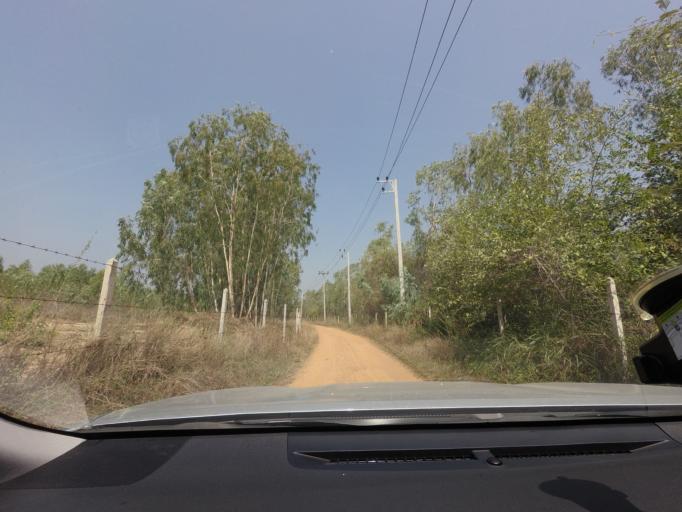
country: TH
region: Prachuap Khiri Khan
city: Prachuap Khiri Khan
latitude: 11.9326
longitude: 99.8181
